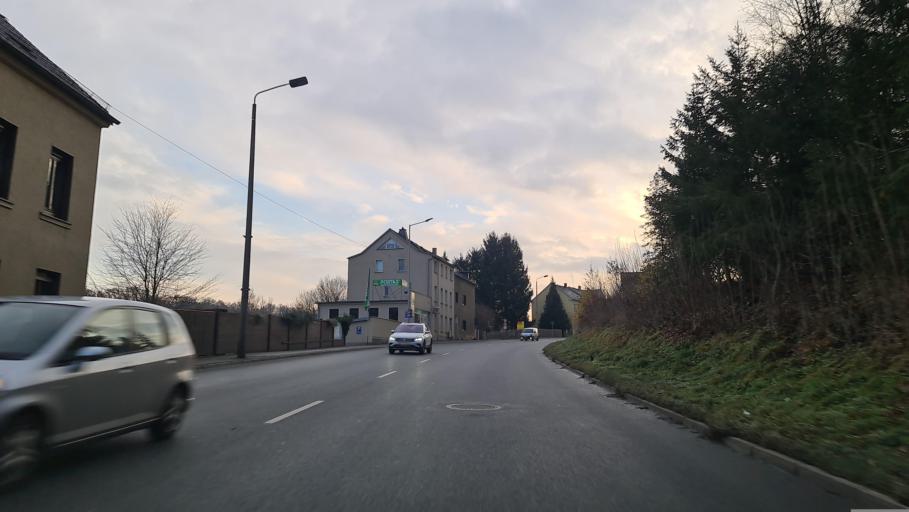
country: DE
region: Saxony
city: Netzschkau
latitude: 50.6160
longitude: 12.2537
